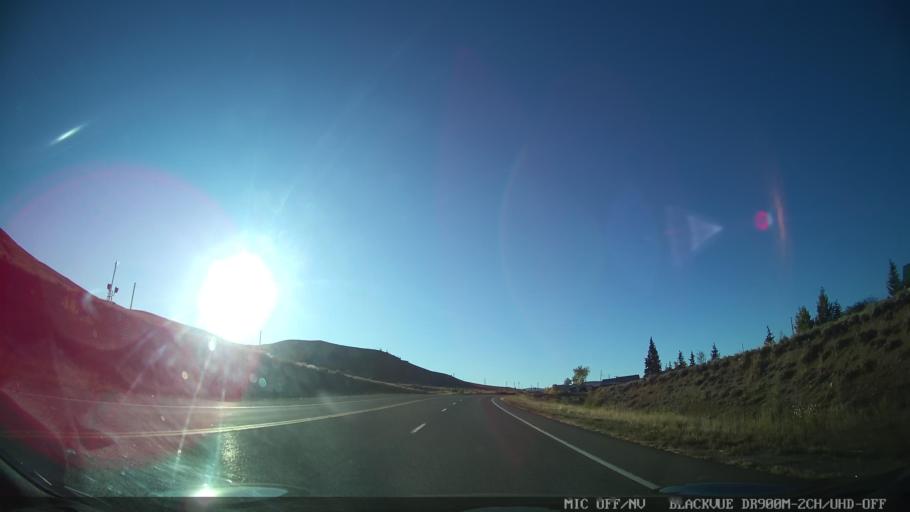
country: US
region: Colorado
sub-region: Grand County
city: Hot Sulphur Springs
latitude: 40.0597
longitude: -106.1771
